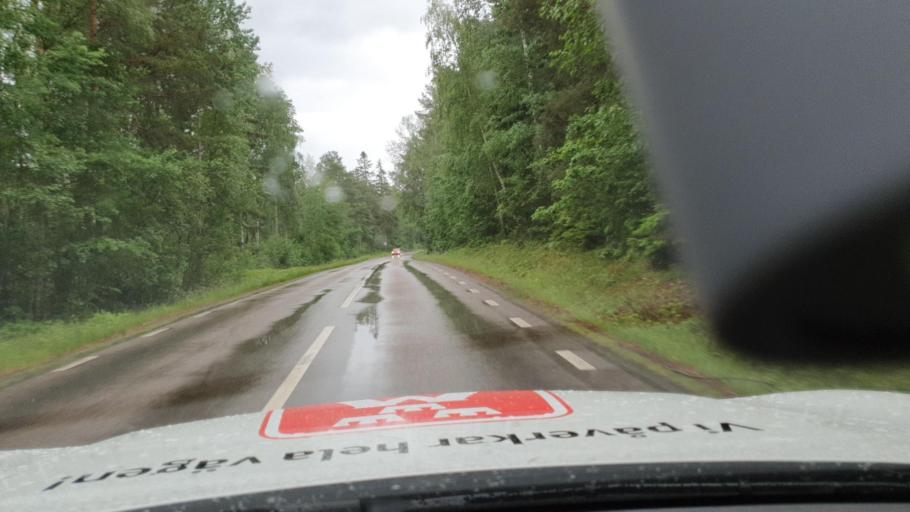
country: SE
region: Vaestra Goetaland
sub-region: Mariestads Kommun
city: Mariestad
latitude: 58.7630
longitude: 13.9099
